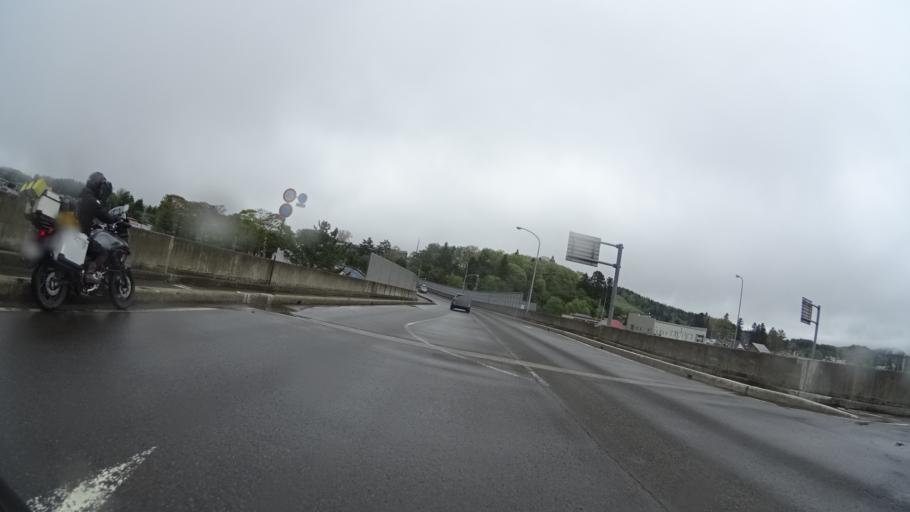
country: JP
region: Nagano
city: Nagano-shi
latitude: 36.8069
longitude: 138.1990
